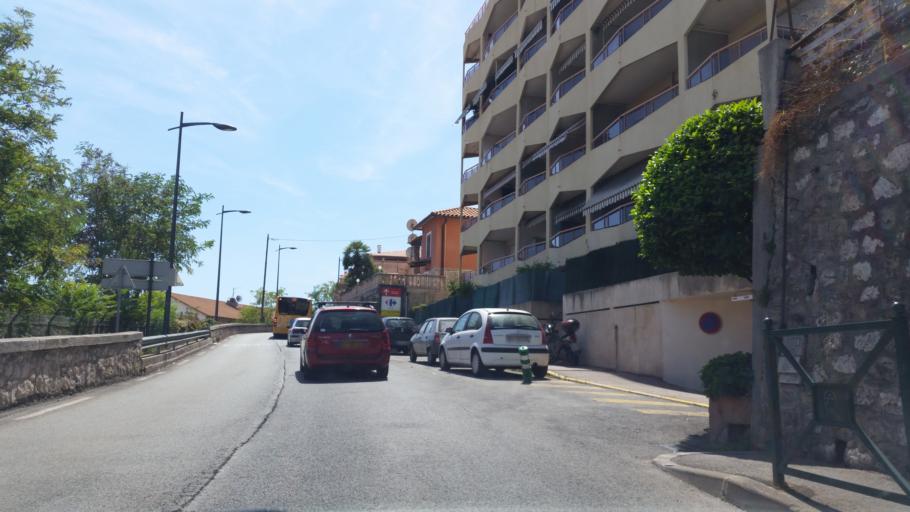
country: FR
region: Provence-Alpes-Cote d'Azur
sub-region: Departement des Alpes-Maritimes
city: Roquebrune-Cap-Martin
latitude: 43.7622
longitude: 7.4785
